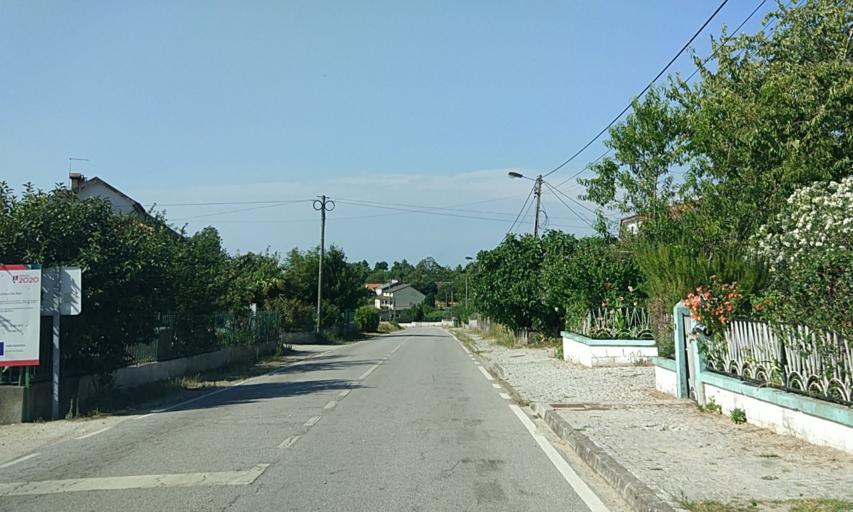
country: PT
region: Vila Real
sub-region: Murca
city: Murca
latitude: 41.3205
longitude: -7.4619
